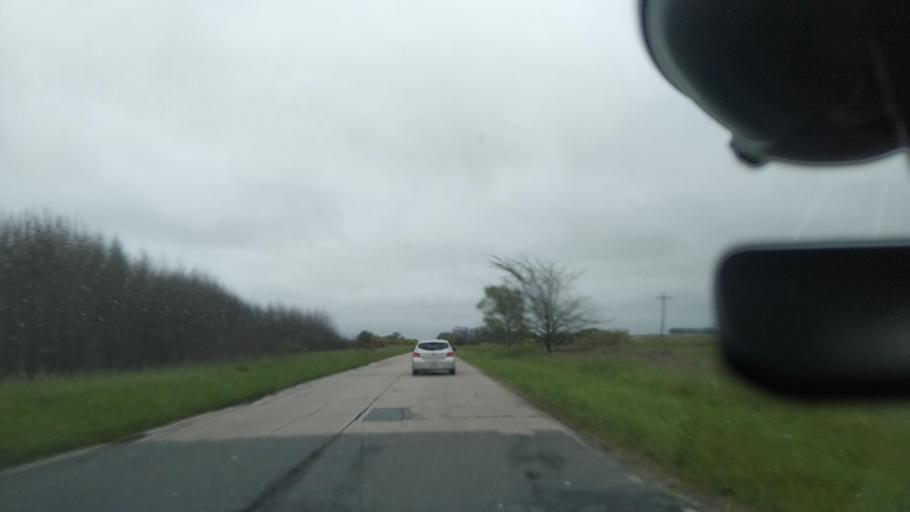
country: AR
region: Buenos Aires
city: Veronica
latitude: -35.5881
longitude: -57.2707
